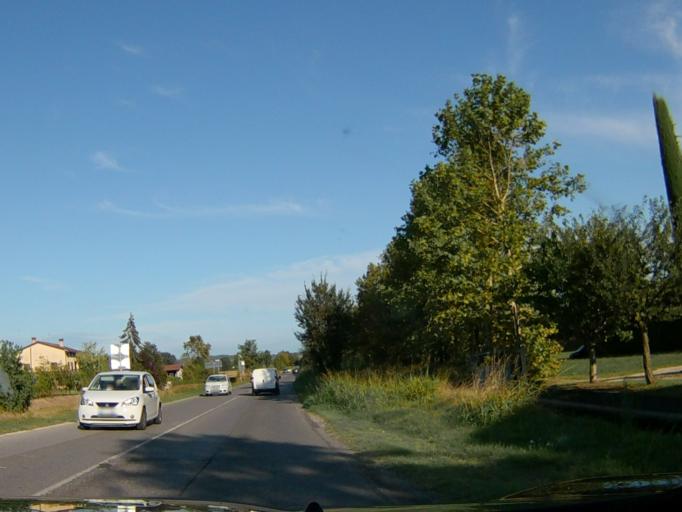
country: IT
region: Lombardy
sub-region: Provincia di Brescia
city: Ponte San Marco
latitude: 45.4747
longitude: 10.4185
